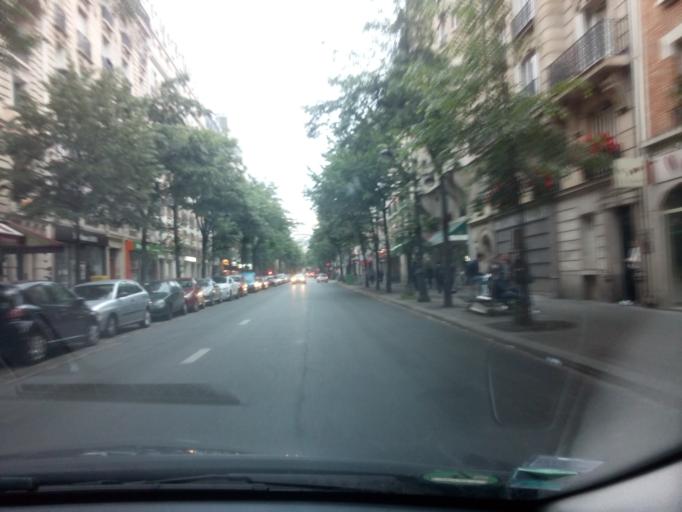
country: FR
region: Ile-de-France
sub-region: Departement des Hauts-de-Seine
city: Vanves
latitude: 48.8391
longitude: 2.2925
